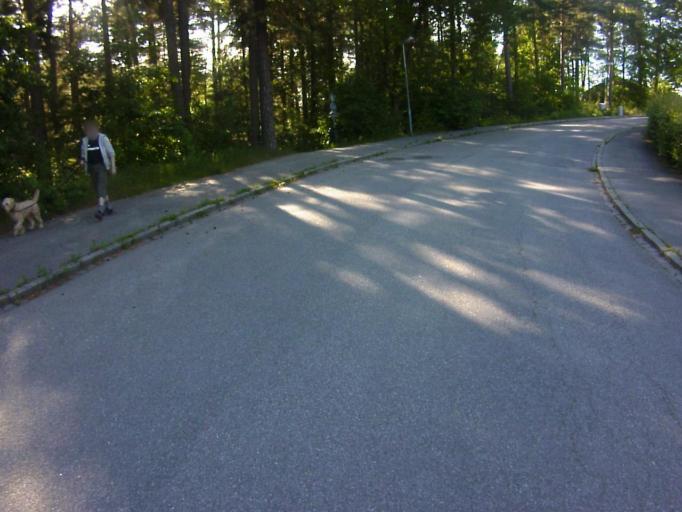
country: SE
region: Soedermanland
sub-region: Eskilstuna Kommun
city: Eskilstuna
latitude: 59.3596
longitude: 16.4906
